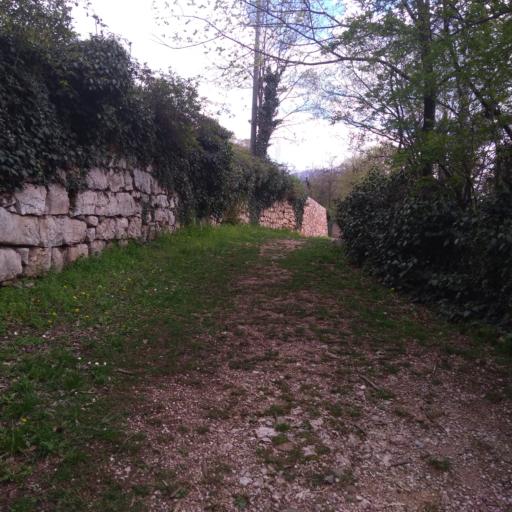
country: IT
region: Trentino-Alto Adige
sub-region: Provincia di Trento
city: Trento
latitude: 46.0911
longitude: 11.1221
